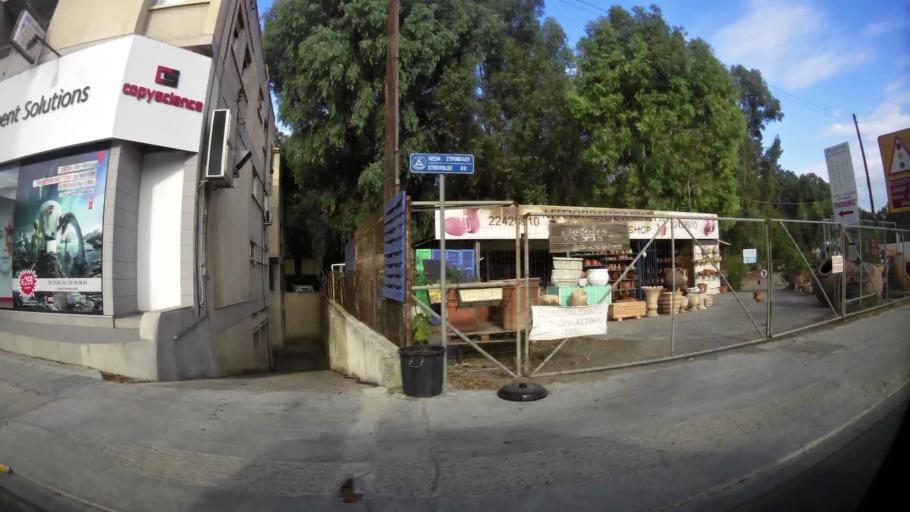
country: CY
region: Lefkosia
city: Nicosia
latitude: 35.1477
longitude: 33.3457
